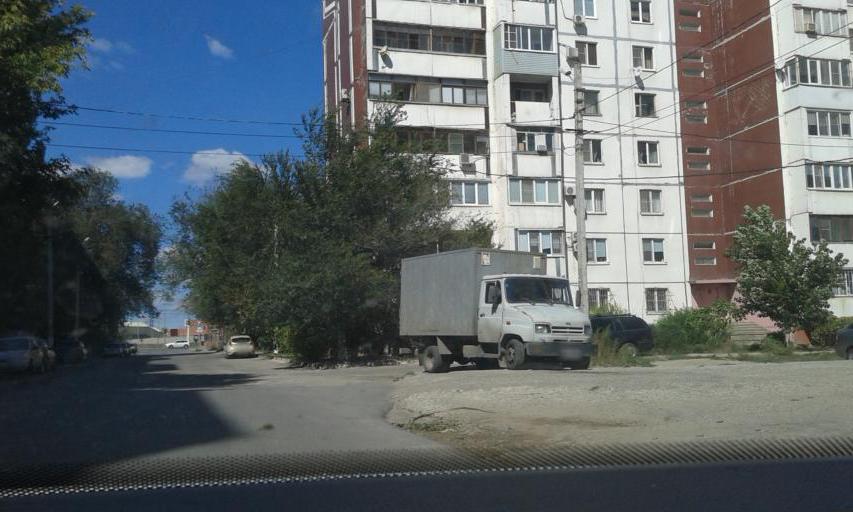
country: RU
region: Volgograd
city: Volgograd
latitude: 48.6794
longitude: 44.4743
